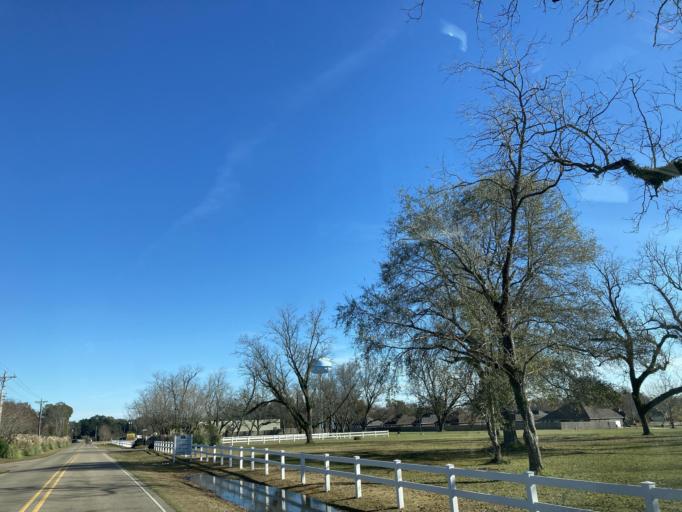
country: US
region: Mississippi
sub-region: Forrest County
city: Petal
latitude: 31.3215
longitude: -89.1874
